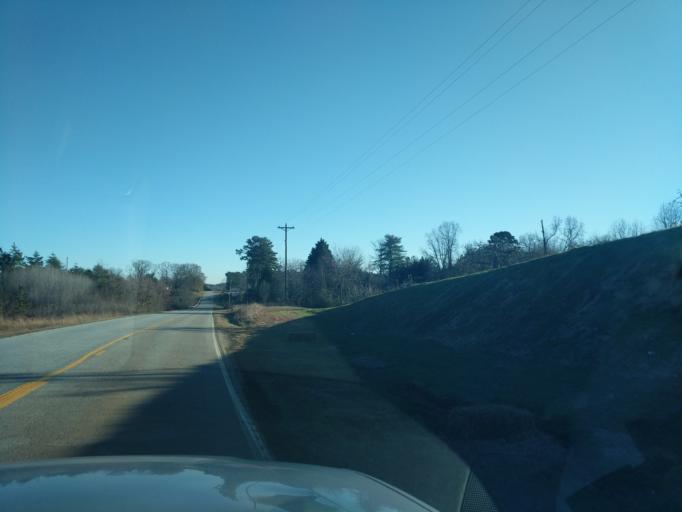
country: US
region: Georgia
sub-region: Rabun County
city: Clayton
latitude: 34.7980
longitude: -83.2708
